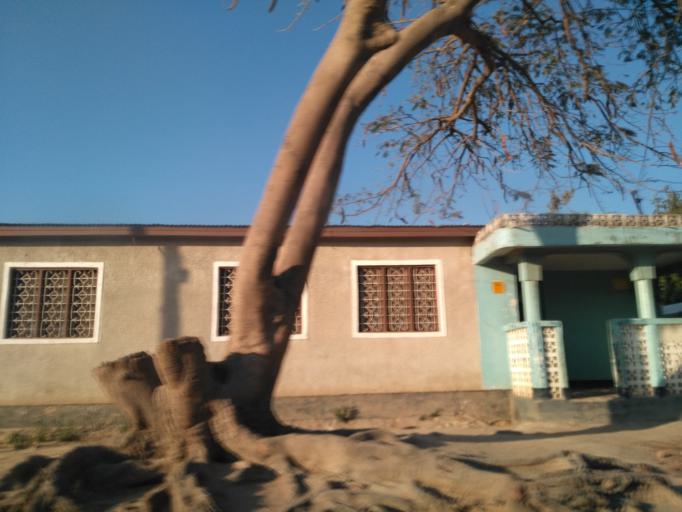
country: TZ
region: Dodoma
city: Dodoma
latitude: -6.1728
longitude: 35.7347
